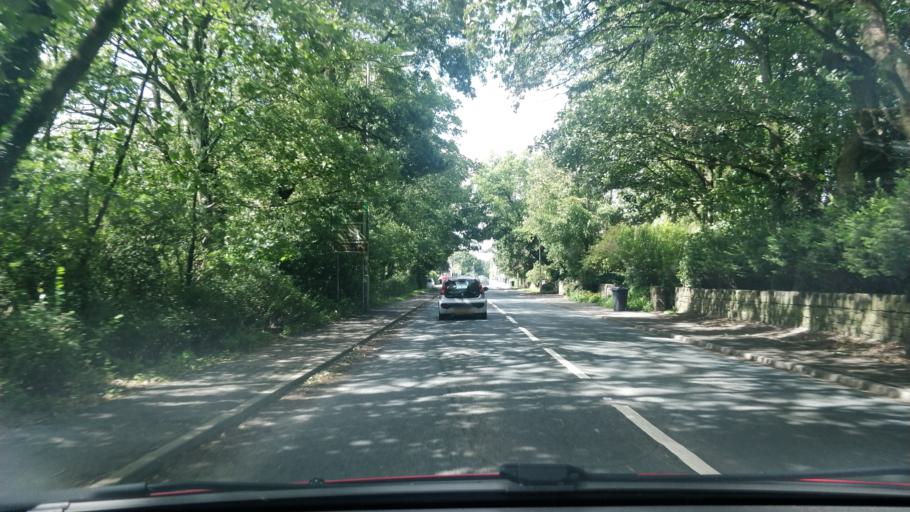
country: GB
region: England
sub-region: Lancashire
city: Appley Bridge
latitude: 53.5916
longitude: -2.7218
